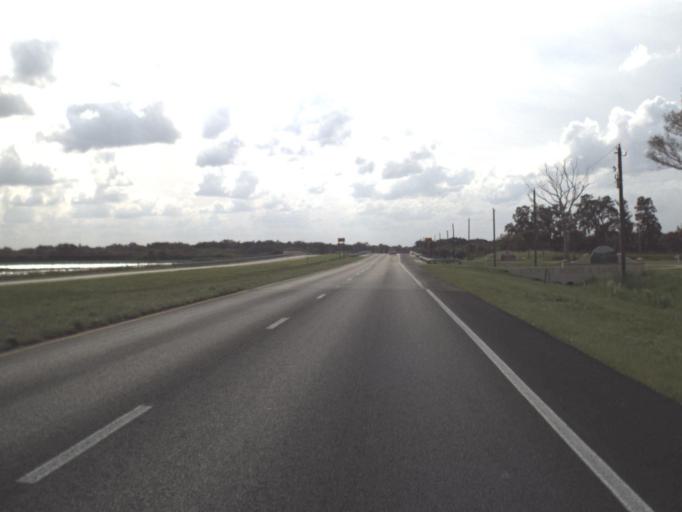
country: US
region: Florida
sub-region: Hendry County
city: Port LaBelle
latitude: 26.7633
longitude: -81.3971
